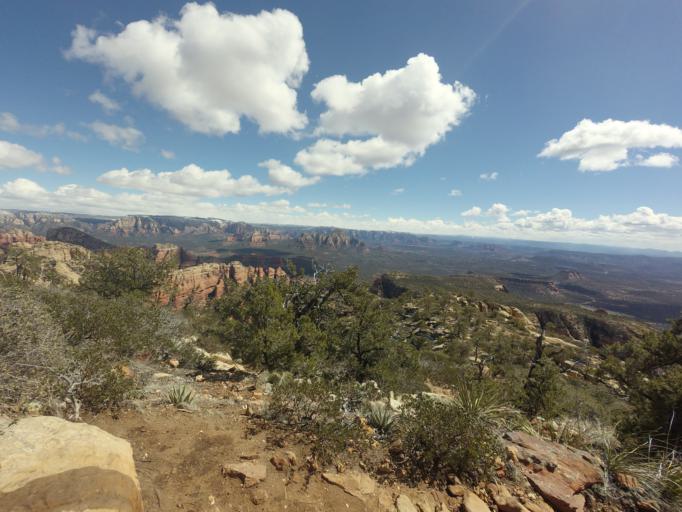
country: US
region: Arizona
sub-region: Yavapai County
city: West Sedona
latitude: 34.9138
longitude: -111.8810
